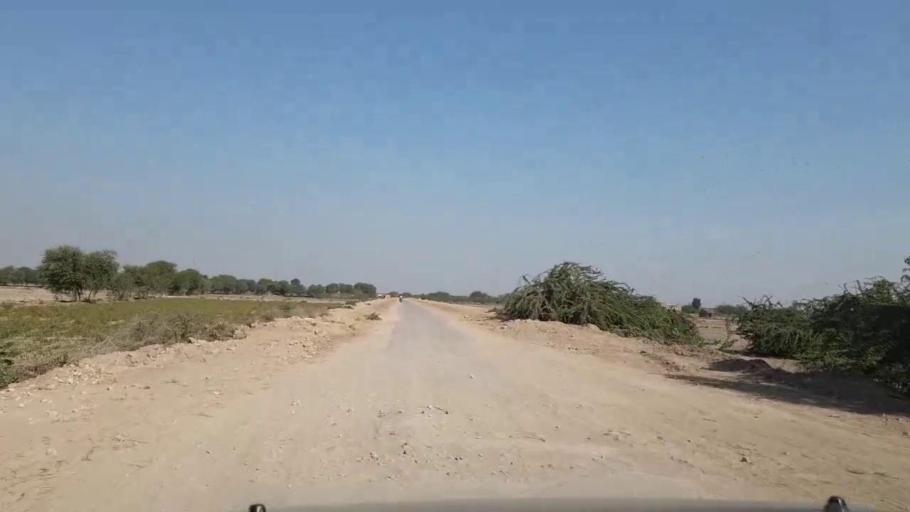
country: PK
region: Sindh
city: Digri
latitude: 24.9562
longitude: 69.1111
